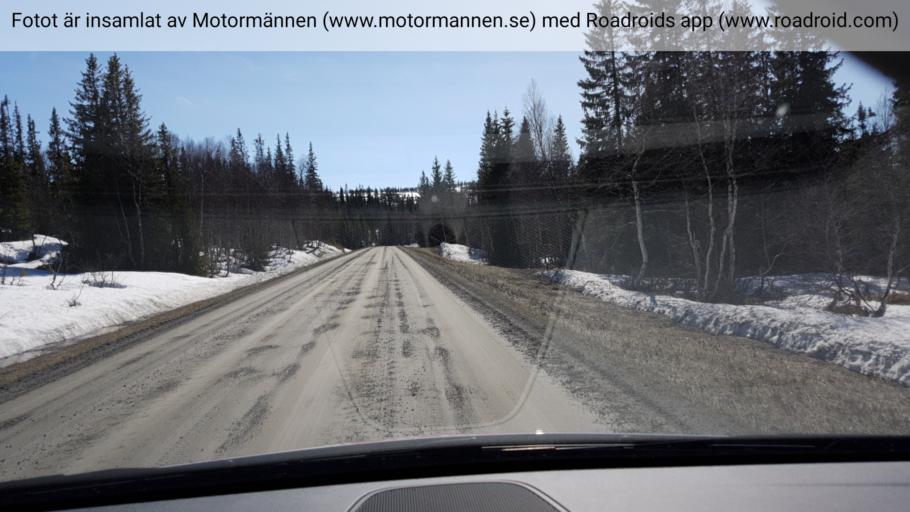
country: NO
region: Nord-Trondelag
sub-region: Snasa
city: Snaase
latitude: 63.7012
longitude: 12.3478
